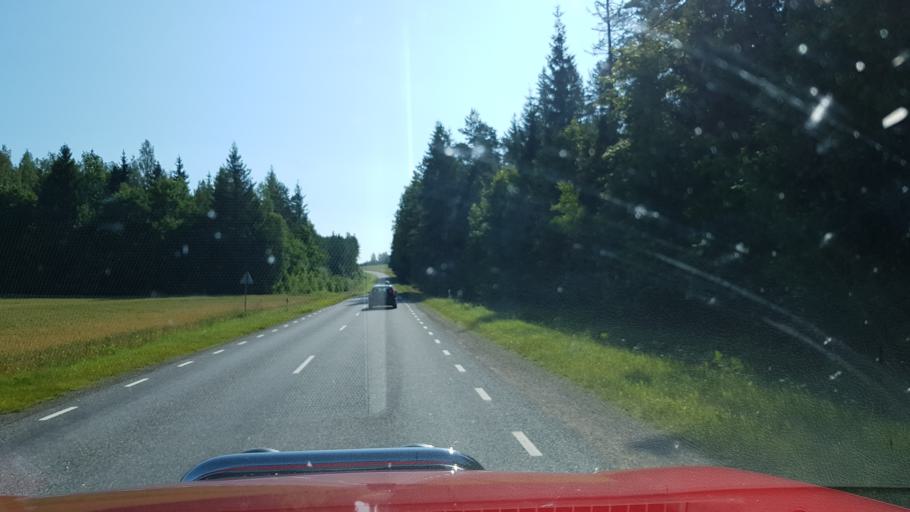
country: EE
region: Vorumaa
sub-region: Voru linn
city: Voru
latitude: 57.9760
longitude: 26.7964
